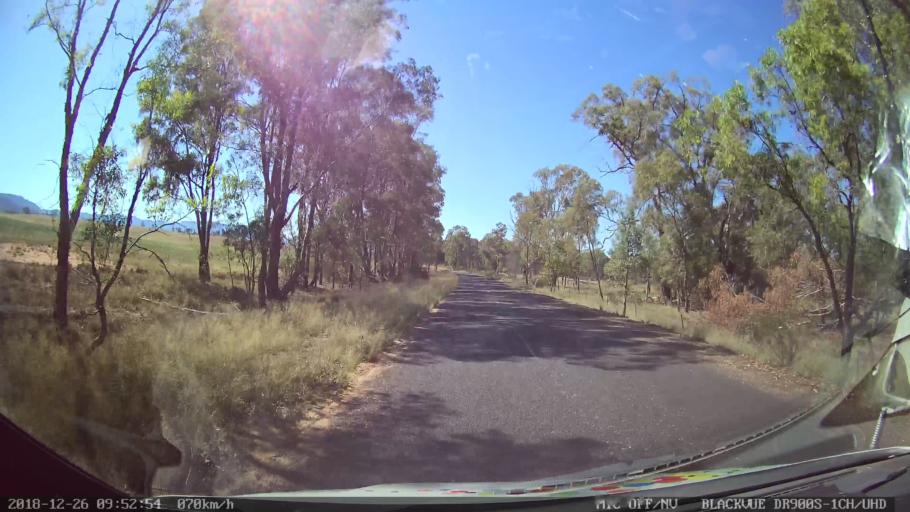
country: AU
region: New South Wales
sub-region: Mid-Western Regional
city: Kandos
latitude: -33.0154
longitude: 150.1508
